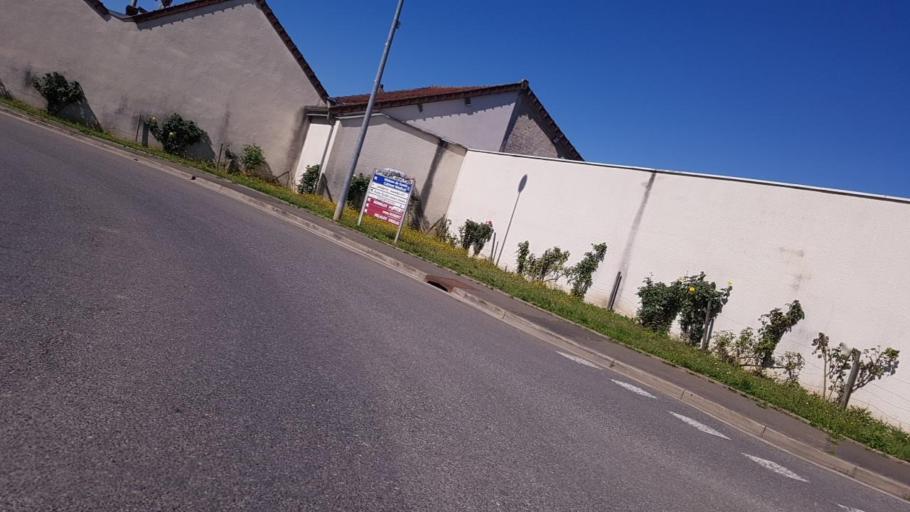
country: FR
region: Picardie
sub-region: Departement de l'Aisne
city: Charly-sur-Marne
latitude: 48.9799
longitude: 3.2869
